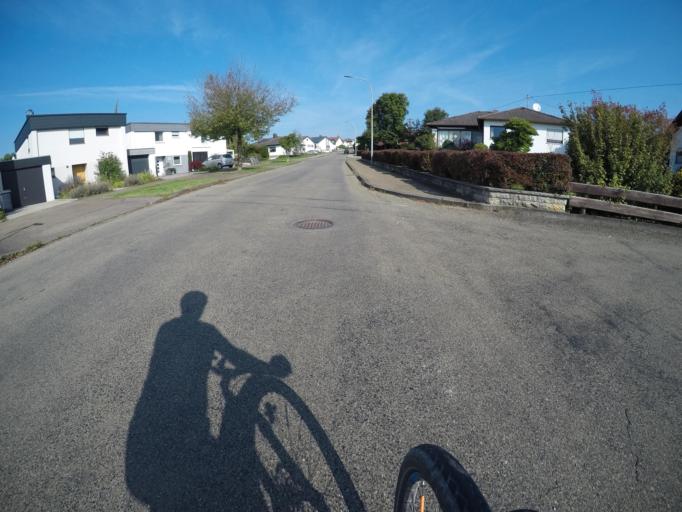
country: DE
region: Baden-Wuerttemberg
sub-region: Regierungsbezirk Stuttgart
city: Gerstetten
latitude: 48.6245
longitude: 10.0082
